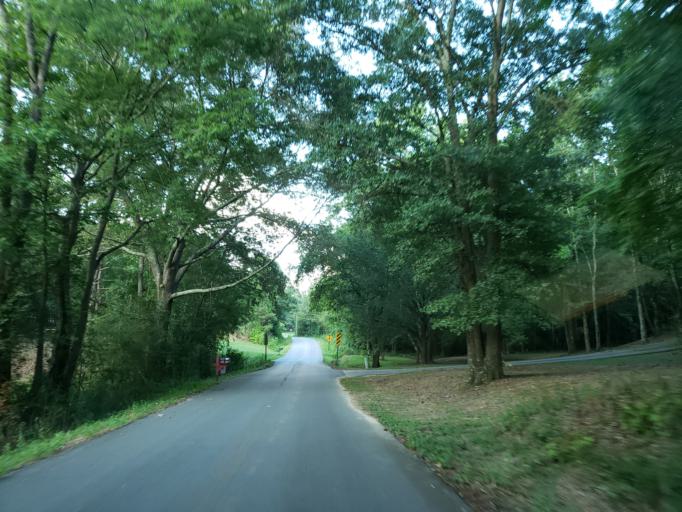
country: US
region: Georgia
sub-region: Bartow County
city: Euharlee
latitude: 34.0757
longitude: -84.9461
